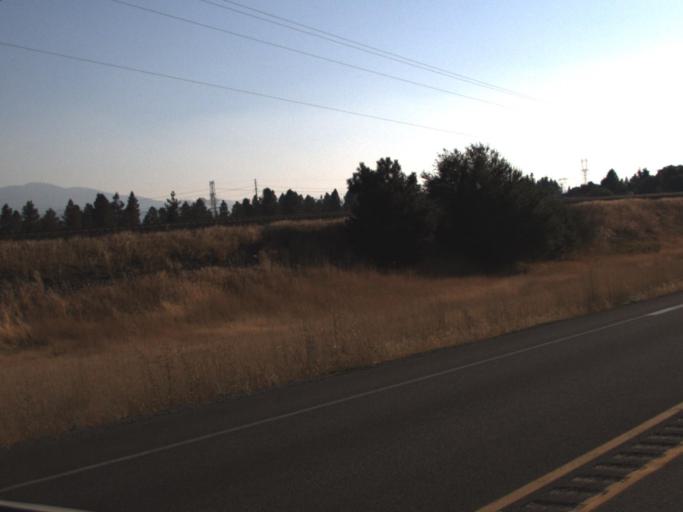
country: US
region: Washington
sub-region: Spokane County
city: Otis Orchards-East Farms
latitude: 47.7254
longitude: -117.0663
